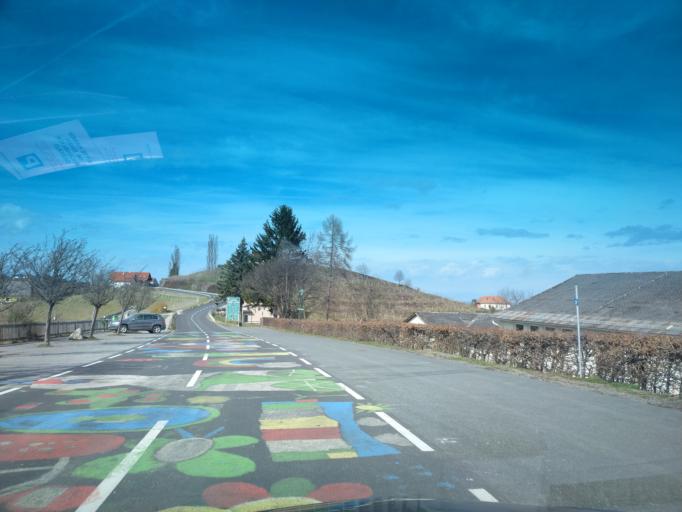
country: AT
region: Styria
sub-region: Politischer Bezirk Leibnitz
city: Kitzeck im Sausal
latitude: 46.7833
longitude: 15.4530
